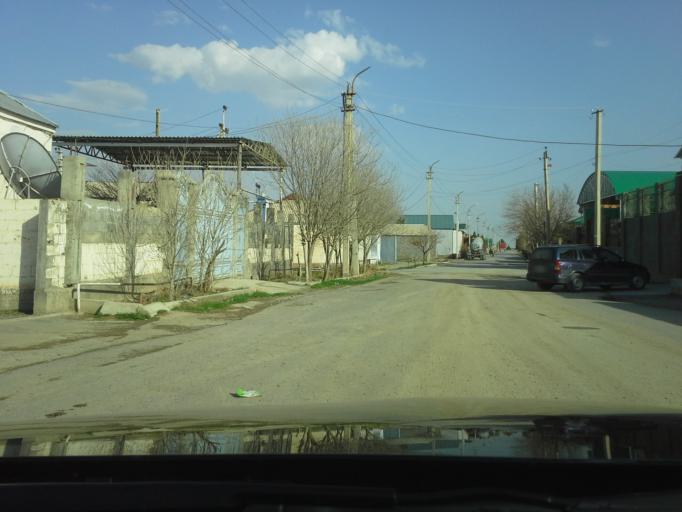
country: TM
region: Ahal
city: Abadan
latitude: 38.0141
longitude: 58.2302
